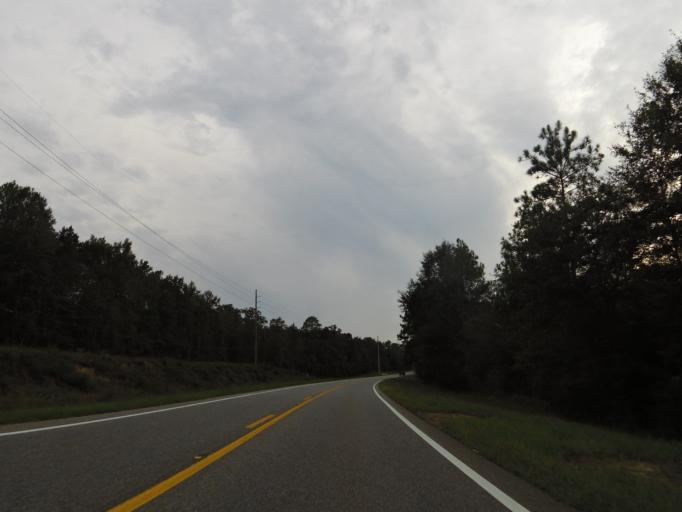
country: US
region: Alabama
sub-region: Baldwin County
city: Bay Minette
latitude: 30.9300
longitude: -87.6883
